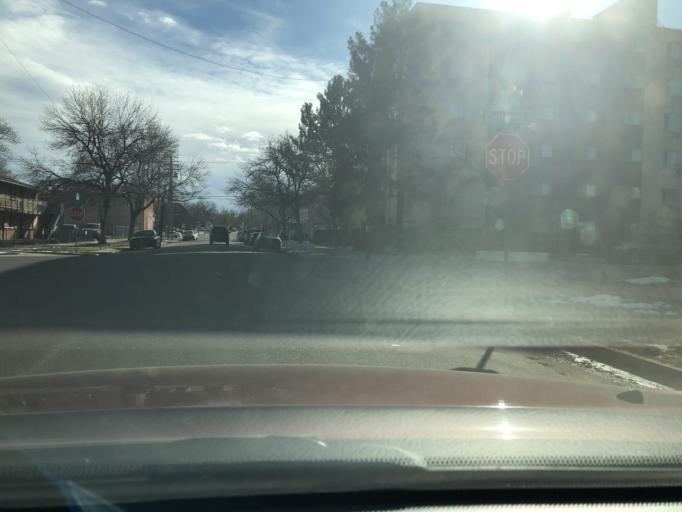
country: US
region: Colorado
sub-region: Denver County
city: Denver
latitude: 39.7565
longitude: -104.9779
